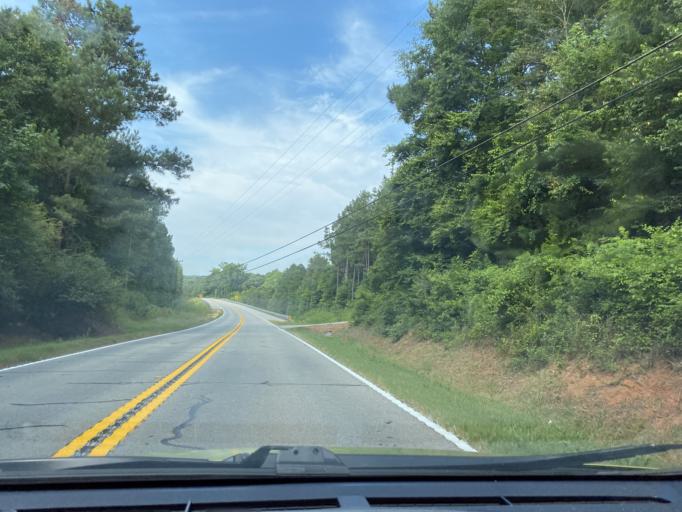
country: US
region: Georgia
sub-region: Coweta County
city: East Newnan
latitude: 33.2858
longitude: -84.6971
